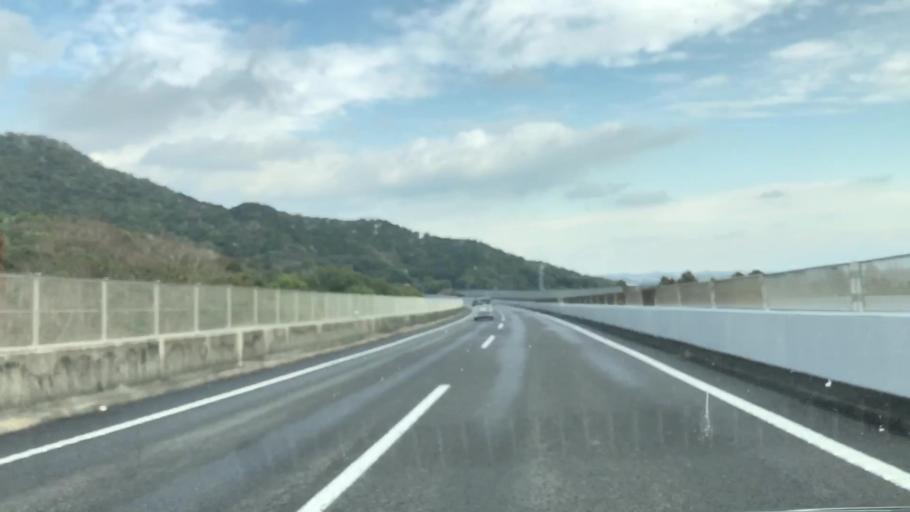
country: JP
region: Saga Prefecture
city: Kanzakimachi-kanzaki
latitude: 33.3387
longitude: 130.3482
